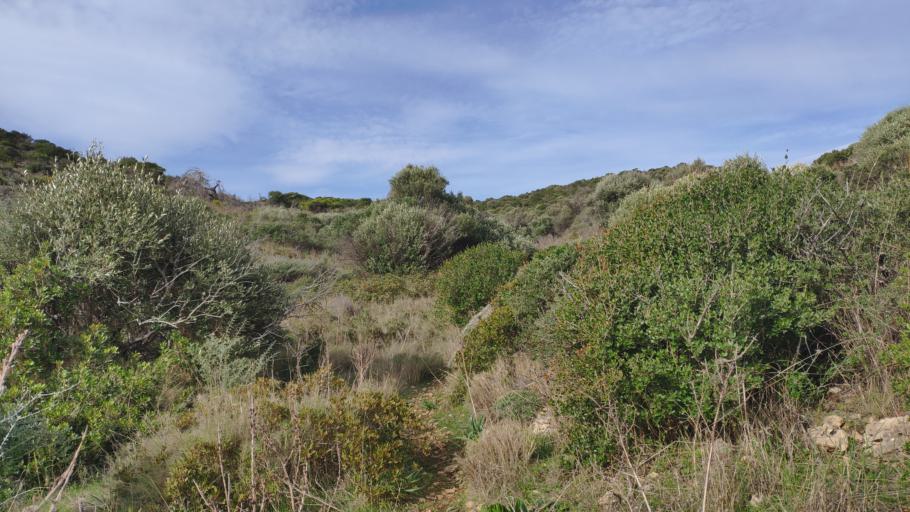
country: GR
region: Attica
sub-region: Nomarchia Anatolikis Attikis
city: Limin Mesoyaias
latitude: 37.9033
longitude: 24.0444
